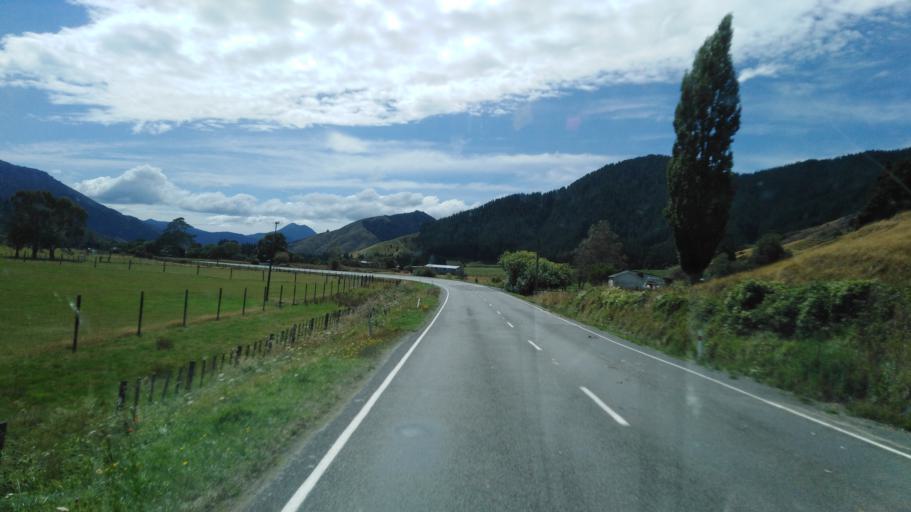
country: NZ
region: Marlborough
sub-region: Marlborough District
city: Blenheim
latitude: -41.3583
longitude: 173.7639
